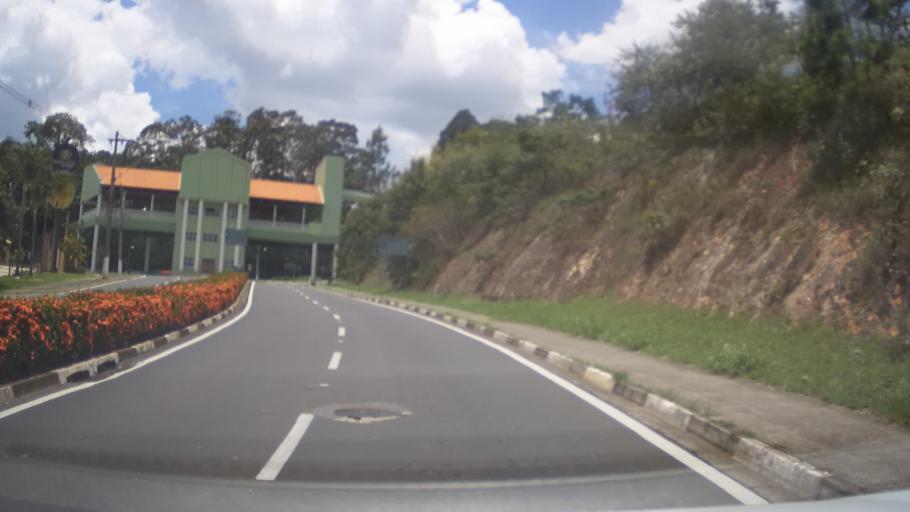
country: BR
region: Sao Paulo
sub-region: Vinhedo
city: Vinhedo
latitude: -23.0247
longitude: -46.9581
